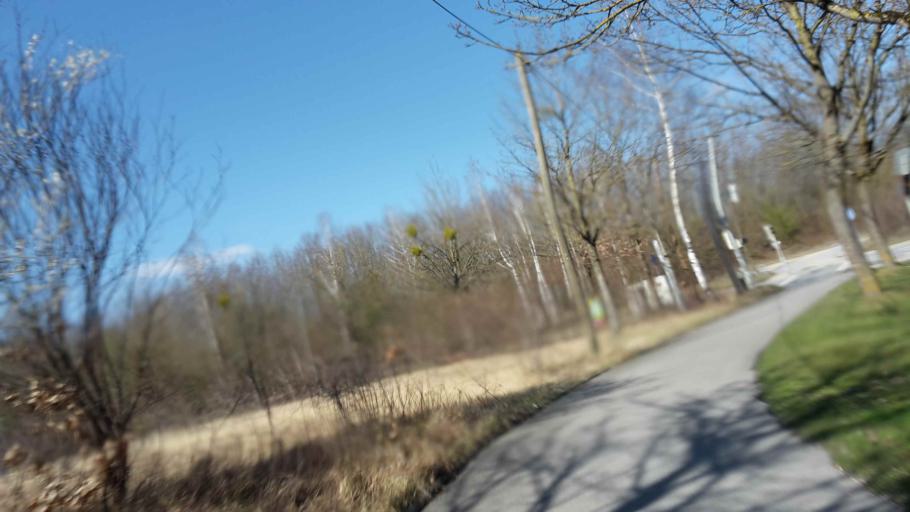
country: DE
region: Bavaria
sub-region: Upper Bavaria
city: Karlsfeld
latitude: 48.1939
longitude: 11.4923
